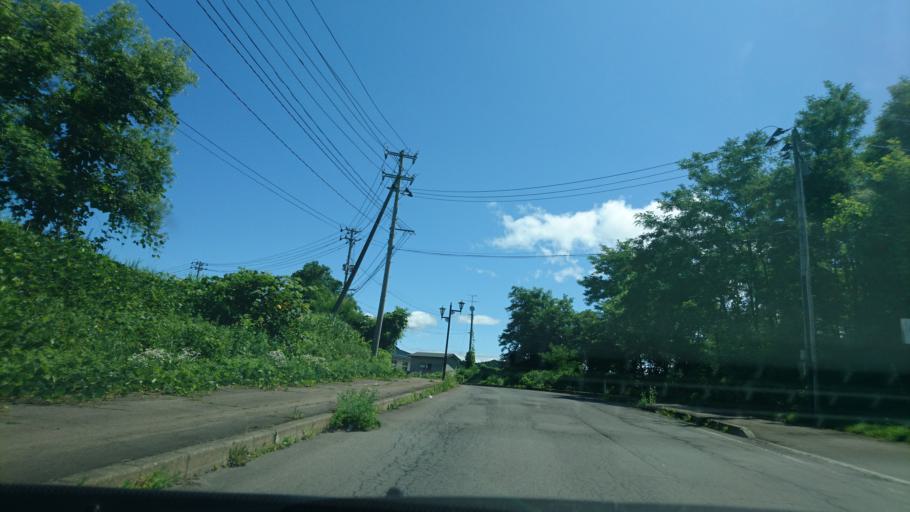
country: JP
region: Akita
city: Kakunodatemachi
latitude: 39.5897
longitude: 140.5679
